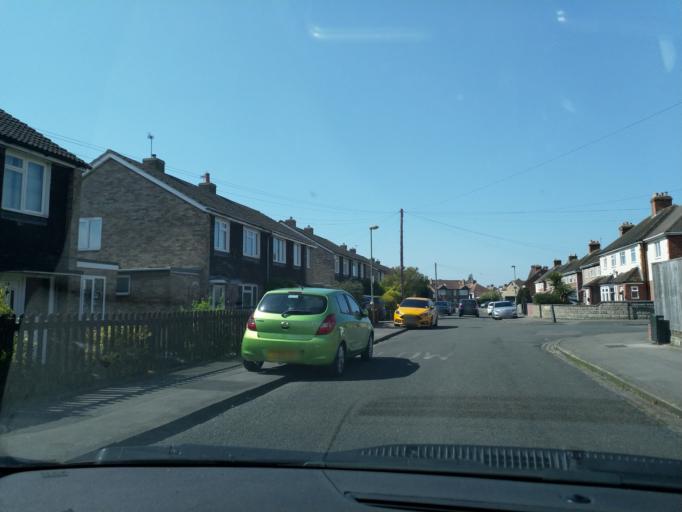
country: GB
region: England
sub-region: Oxfordshire
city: Cowley
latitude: 51.7390
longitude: -1.1998
